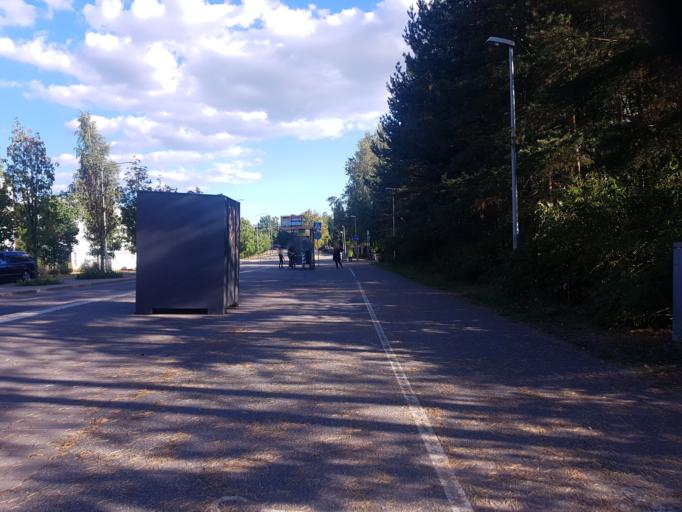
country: FI
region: Uusimaa
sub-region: Helsinki
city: Vantaa
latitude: 60.2640
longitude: 24.9836
